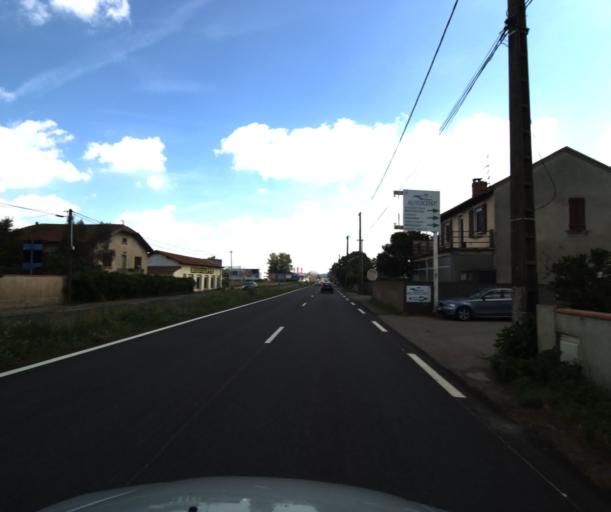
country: FR
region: Midi-Pyrenees
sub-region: Departement de la Haute-Garonne
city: Pinsaguel
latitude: 43.5203
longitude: 1.3916
